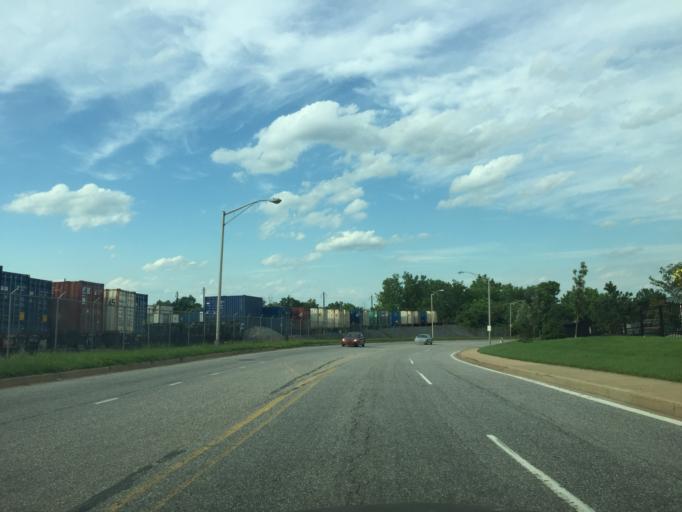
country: US
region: Maryland
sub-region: Baltimore County
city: Rosedale
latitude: 39.2948
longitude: -76.5492
